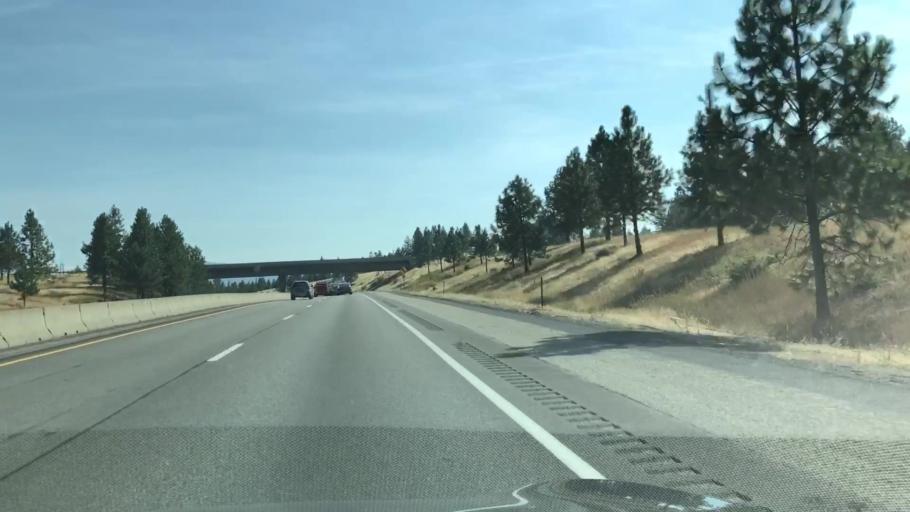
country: US
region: Idaho
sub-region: Kootenai County
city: Coeur d'Alene
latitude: 47.6572
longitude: -116.7278
